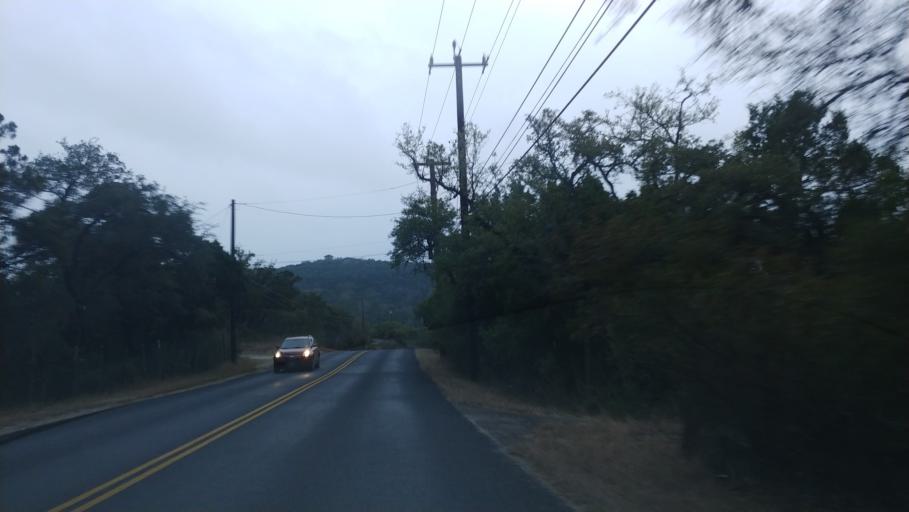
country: US
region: Texas
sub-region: Bexar County
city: Cross Mountain
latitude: 29.6387
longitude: -98.6783
